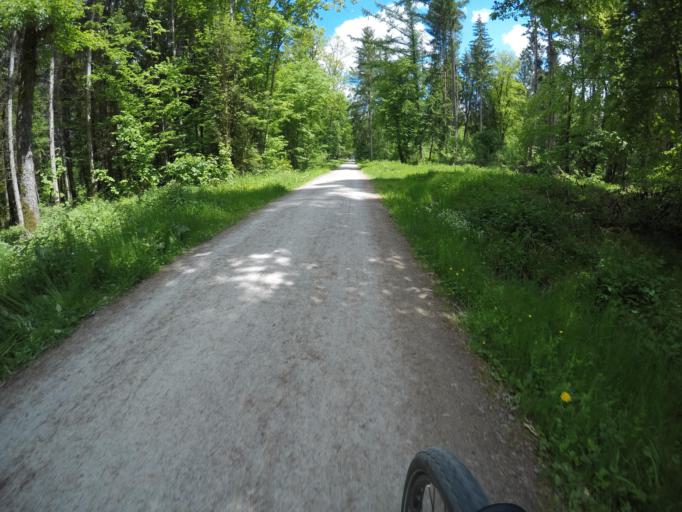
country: DE
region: Baden-Wuerttemberg
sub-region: Regierungsbezirk Stuttgart
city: Gerlingen
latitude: 48.7460
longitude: 9.0748
